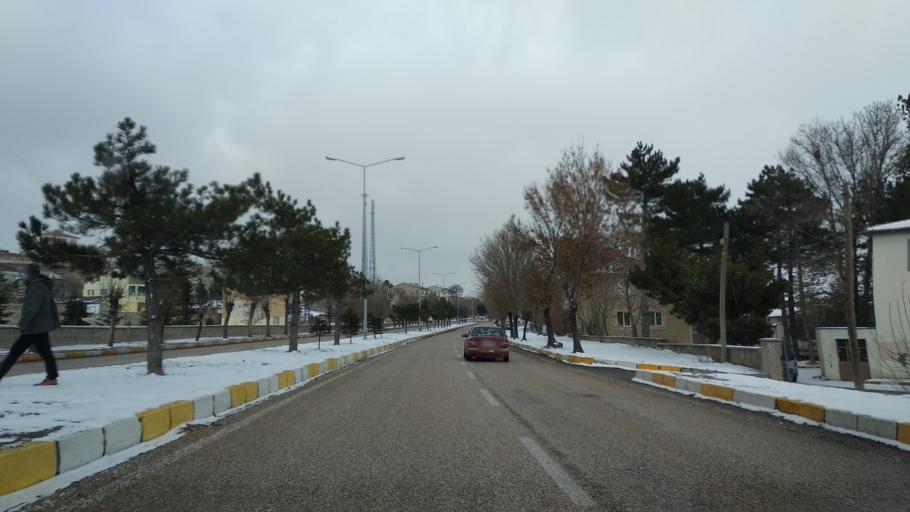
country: TR
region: Kayseri
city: Pinarbasi
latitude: 38.7218
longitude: 36.3878
